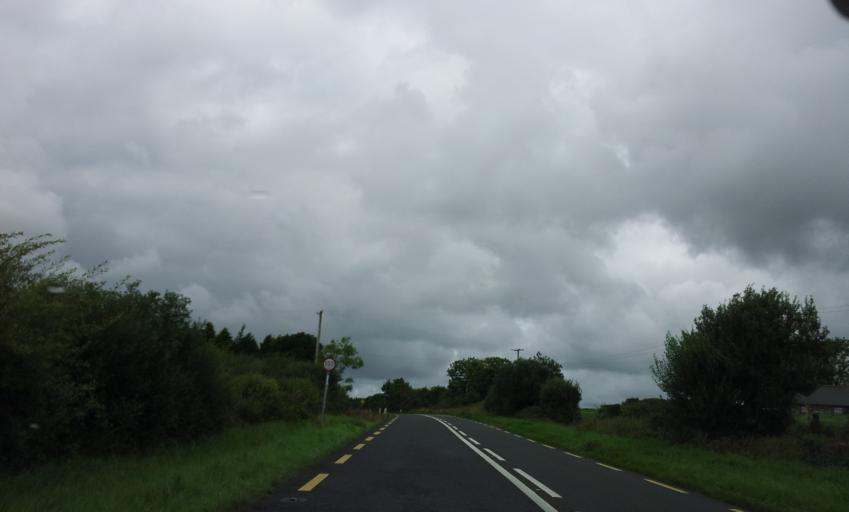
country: IE
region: Munster
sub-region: An Clar
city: Ennis
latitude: 52.8975
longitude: -9.2065
